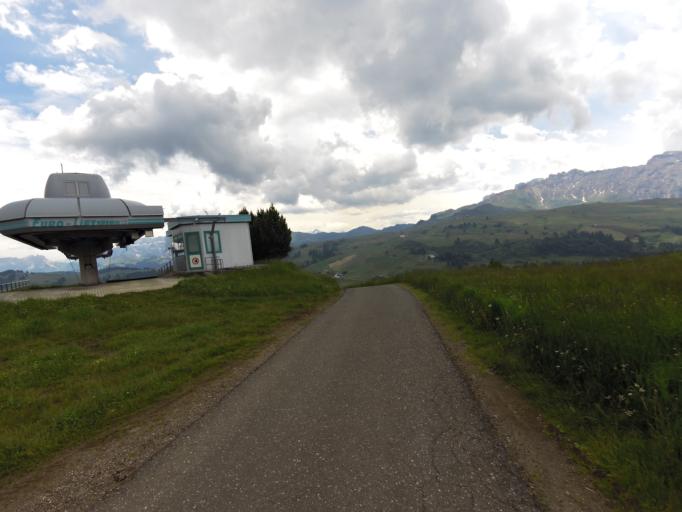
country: IT
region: Trentino-Alto Adige
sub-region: Bolzano
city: Siusi
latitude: 46.5447
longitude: 11.6138
